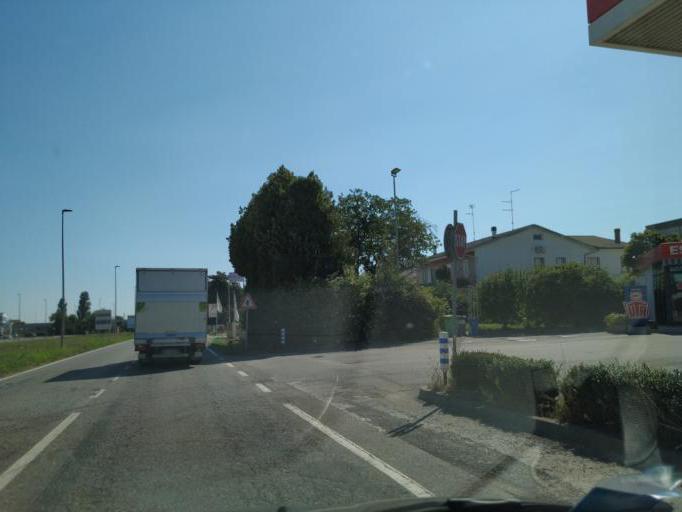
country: IT
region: Emilia-Romagna
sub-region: Provincia di Ferrara
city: Copparo
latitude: 44.8895
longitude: 11.8021
